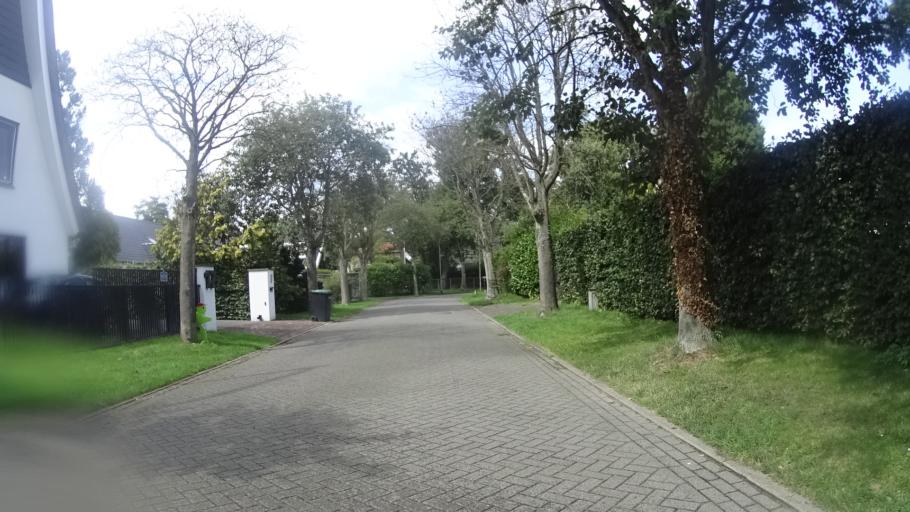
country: NL
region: North Holland
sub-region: Gemeente Alkmaar
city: Alkmaar
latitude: 52.6756
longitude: 4.6969
